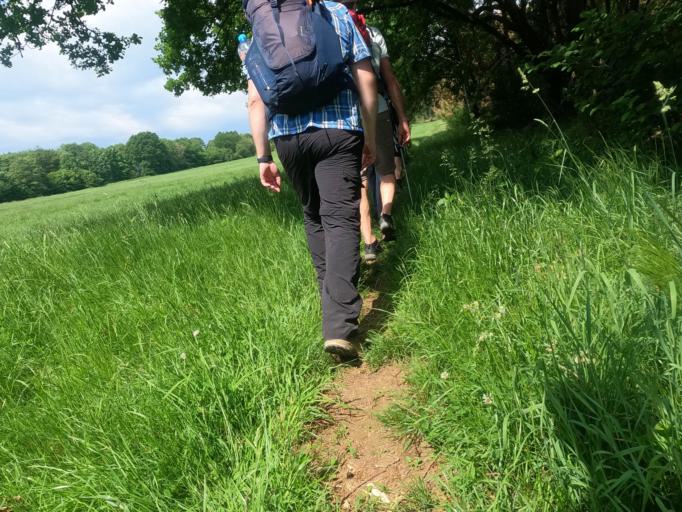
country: DE
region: Rheinland-Pfalz
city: Lochum
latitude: 50.6147
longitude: 7.8712
